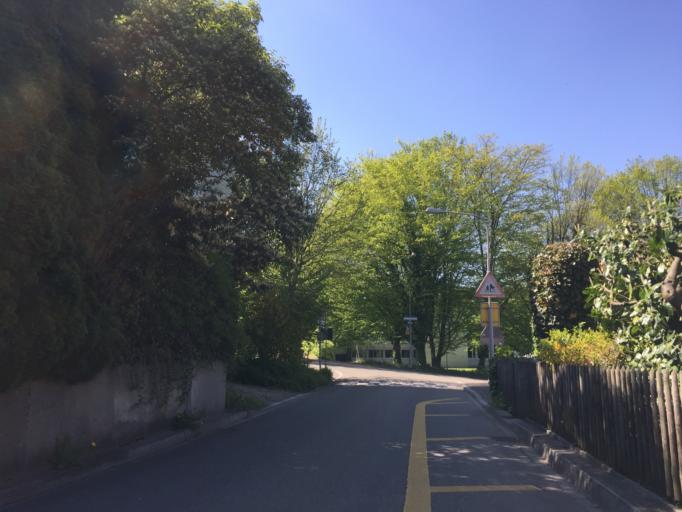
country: CH
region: Zurich
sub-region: Bezirk Zuerich
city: Zuerich (Kreis 12) / Saatlen
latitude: 47.4063
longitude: 8.5565
